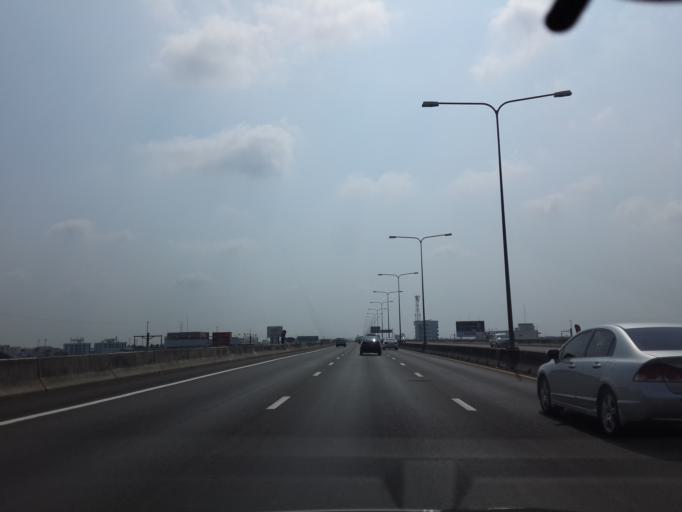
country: TH
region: Samut Prakan
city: Bang Bo District
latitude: 13.6168
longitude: 100.7469
